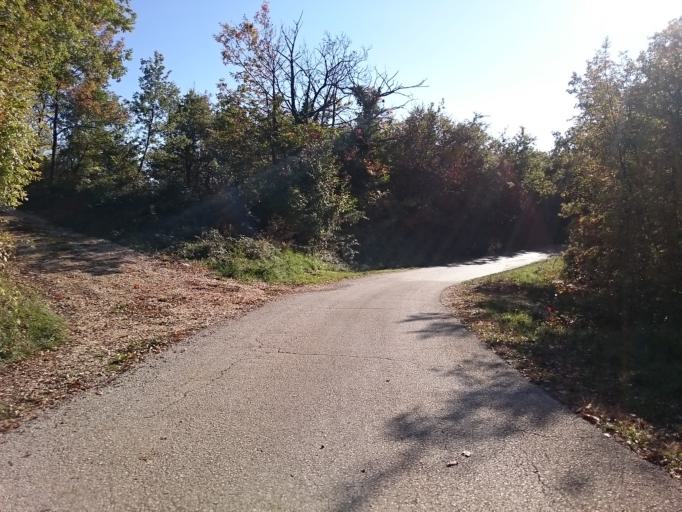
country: HR
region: Istarska
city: Buje
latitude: 45.4238
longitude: 13.7375
